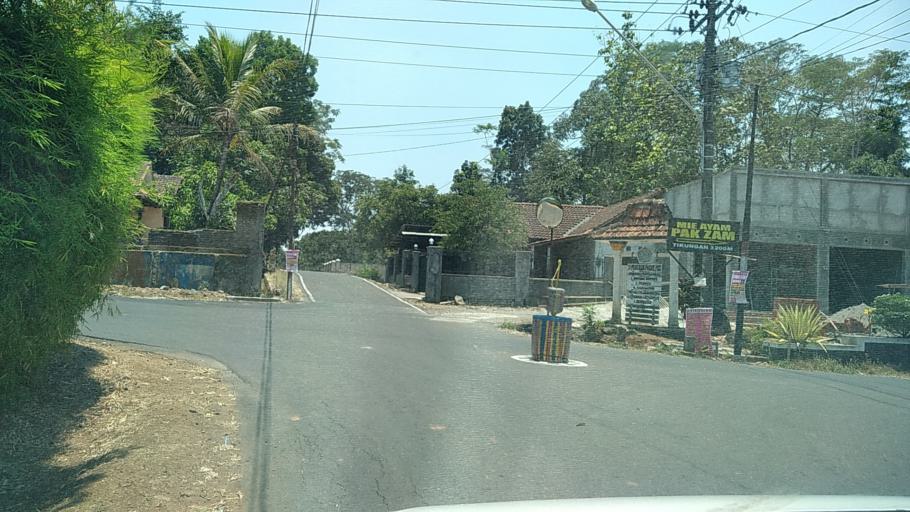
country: ID
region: Central Java
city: Ungaran
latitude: -7.0751
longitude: 110.3658
